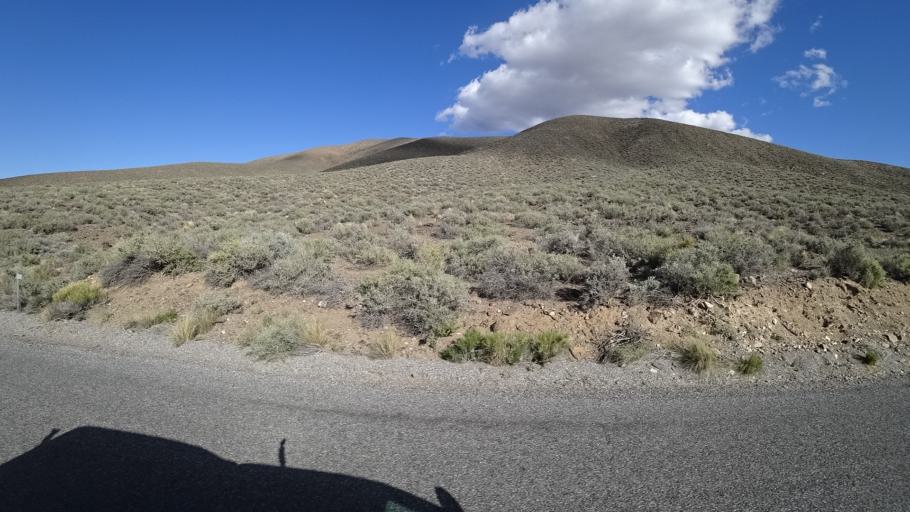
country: US
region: California
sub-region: San Bernardino County
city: Searles Valley
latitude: 36.3252
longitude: -117.1497
